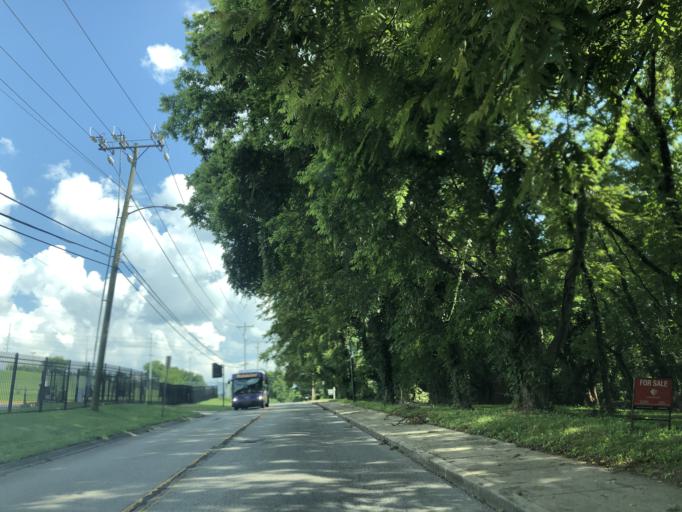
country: US
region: Tennessee
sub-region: Davidson County
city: Nashville
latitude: 36.1648
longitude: -86.8341
